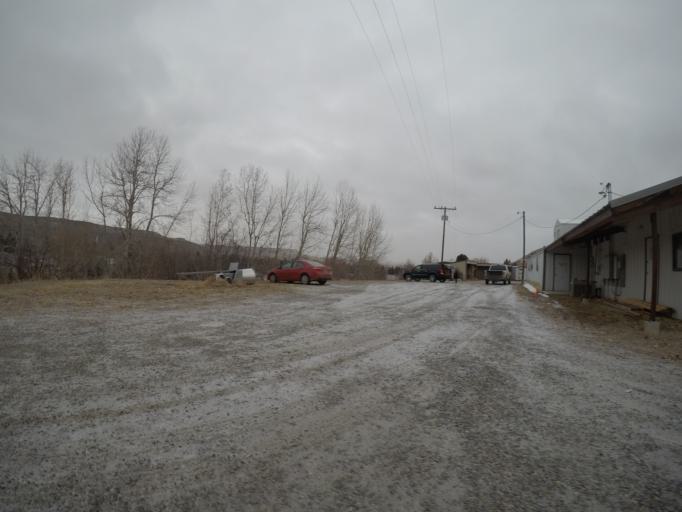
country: US
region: Montana
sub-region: Stillwater County
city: Absarokee
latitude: 45.5139
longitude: -109.4425
